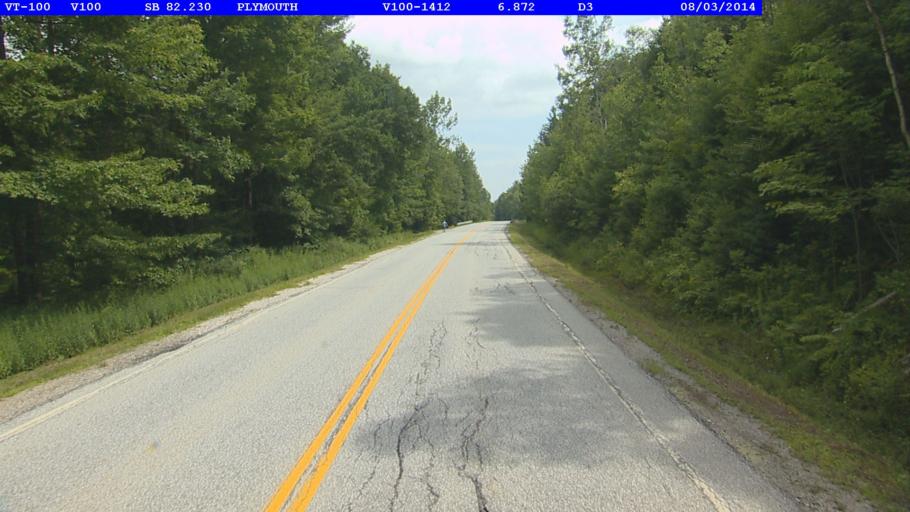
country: US
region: Vermont
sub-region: Rutland County
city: Rutland
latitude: 43.5495
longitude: -72.7534
